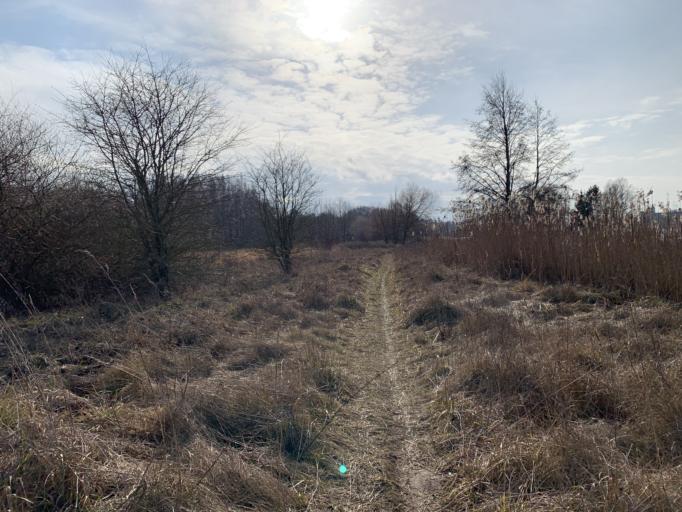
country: BY
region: Minsk
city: Nyasvizh
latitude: 53.2303
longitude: 26.7052
